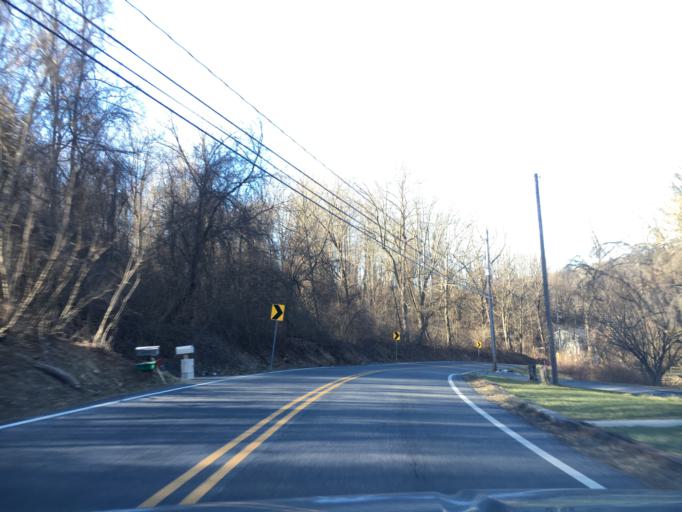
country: US
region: Pennsylvania
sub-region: Berks County
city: South Temple
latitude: 40.4072
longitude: -75.8758
